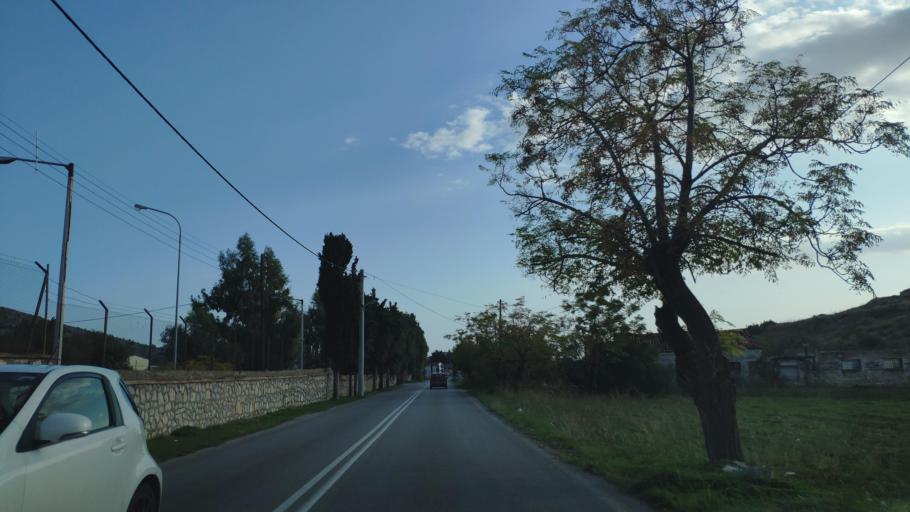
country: GR
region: Attica
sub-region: Nomarchia Dytikis Attikis
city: Megara
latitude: 37.9805
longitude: 23.3550
